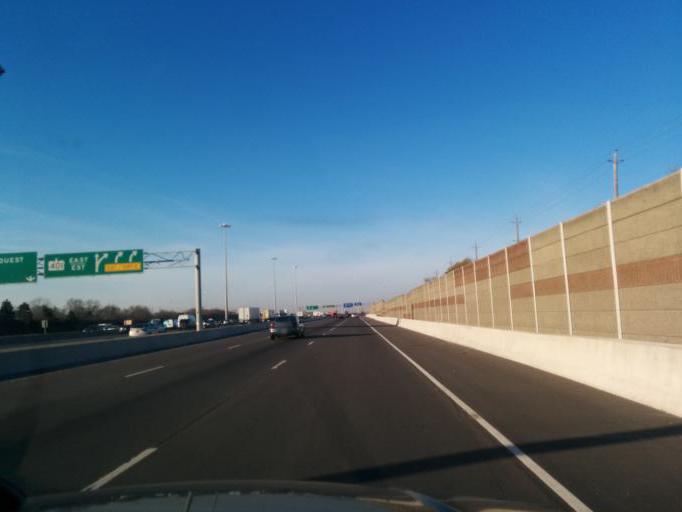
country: CA
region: Ontario
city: Etobicoke
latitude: 43.6642
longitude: -79.5715
